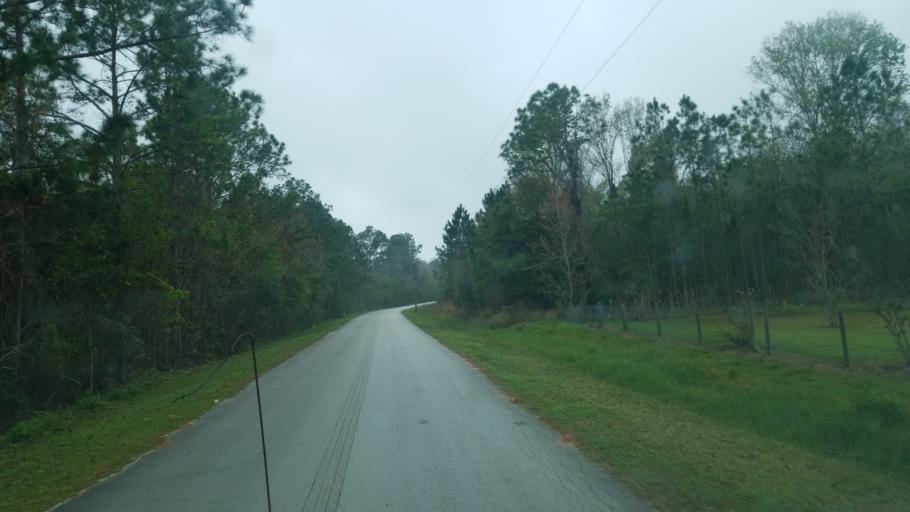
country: US
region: Florida
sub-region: Lake County
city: Groveland
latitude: 28.3886
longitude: -81.8362
